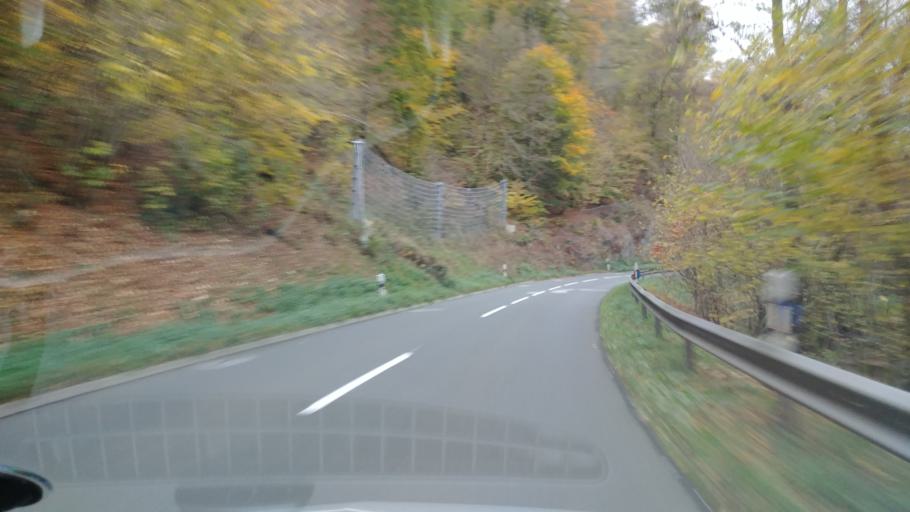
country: DE
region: Rheinland-Pfalz
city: Burgschwalbach
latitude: 50.2312
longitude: 8.1093
